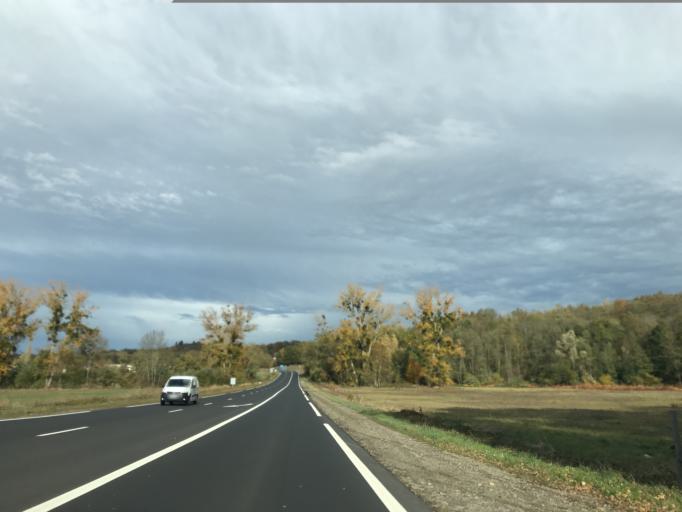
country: FR
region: Auvergne
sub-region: Departement du Puy-de-Dome
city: Peschadoires
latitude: 45.8481
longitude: 3.5062
